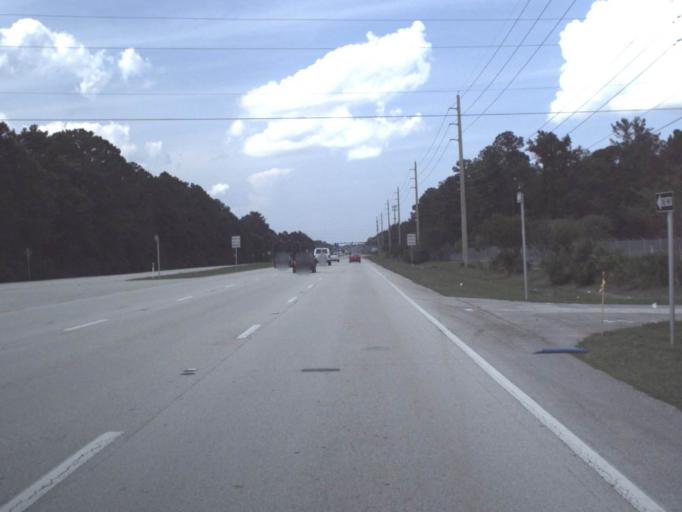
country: US
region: Florida
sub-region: Clay County
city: Orange Park
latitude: 30.2148
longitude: -81.7037
